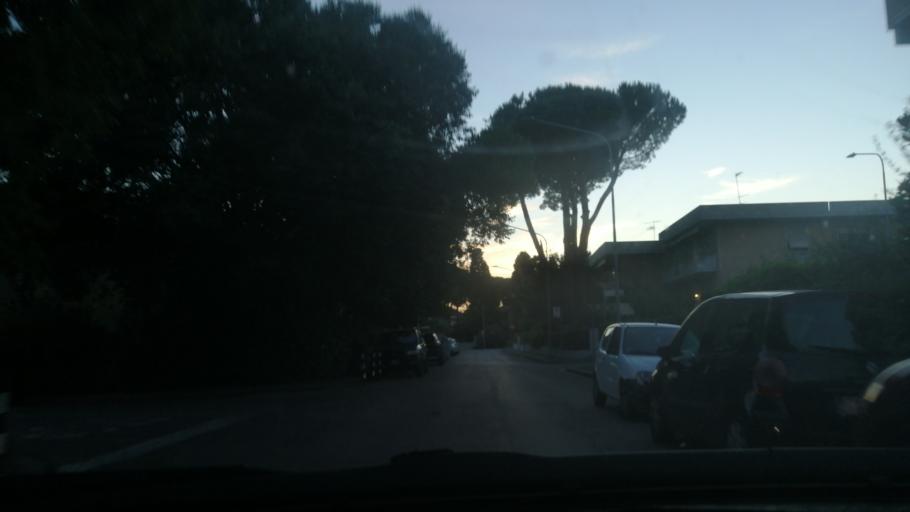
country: IT
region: Tuscany
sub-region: Province of Florence
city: Sesto Fiorentino
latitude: 43.8426
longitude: 11.1983
